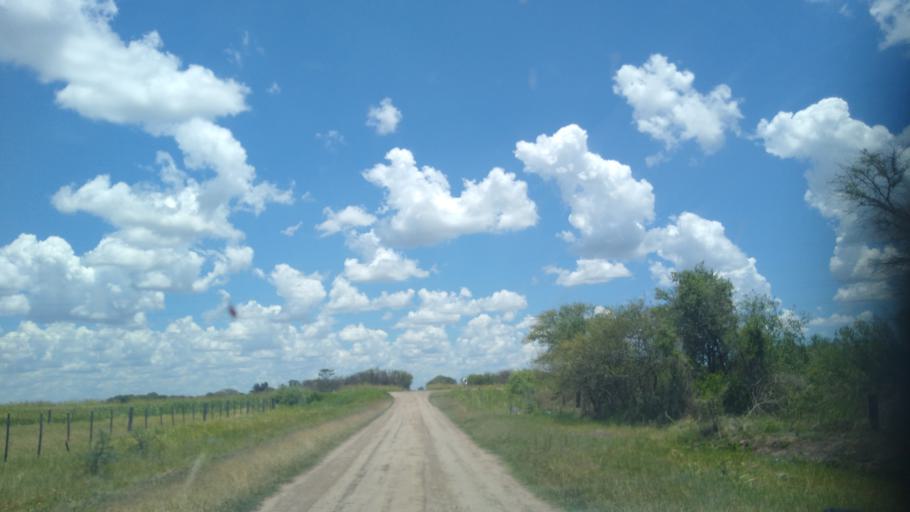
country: AR
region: Chaco
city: Presidencia Roque Saenz Pena
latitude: -26.7323
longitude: -60.3822
